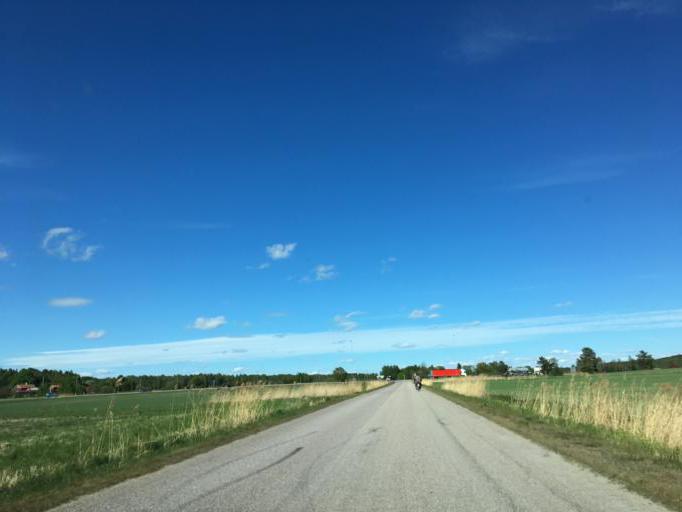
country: SE
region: Soedermanland
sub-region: Eskilstuna Kommun
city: Kvicksund
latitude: 59.4059
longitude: 16.2419
